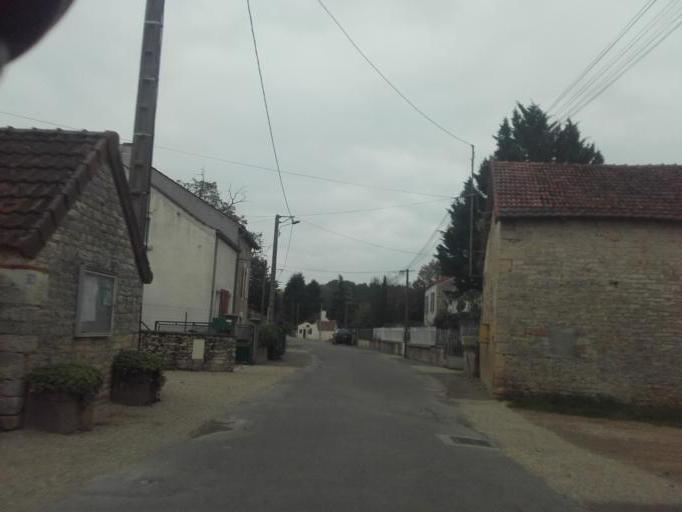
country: FR
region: Bourgogne
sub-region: Departement de Saone-et-Loire
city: Demigny
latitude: 46.9296
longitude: 4.8002
